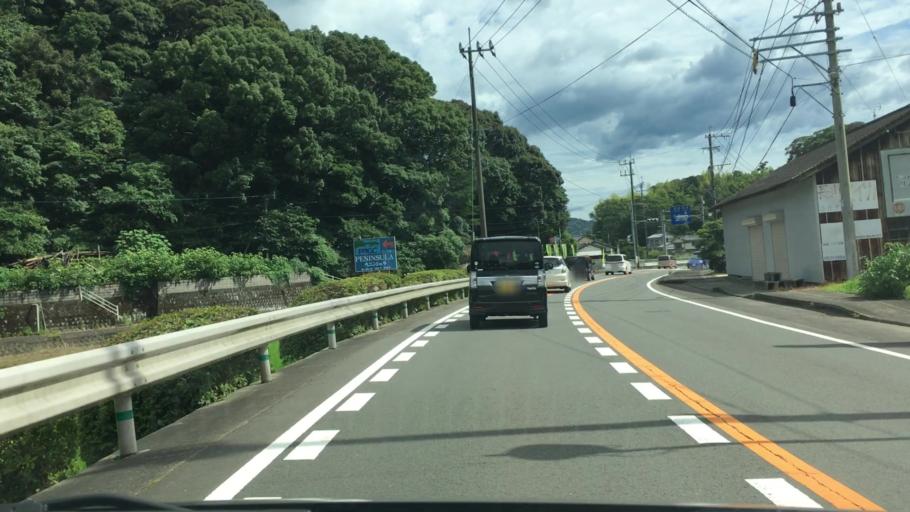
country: JP
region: Nagasaki
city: Togitsu
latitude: 32.9534
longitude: 129.7856
